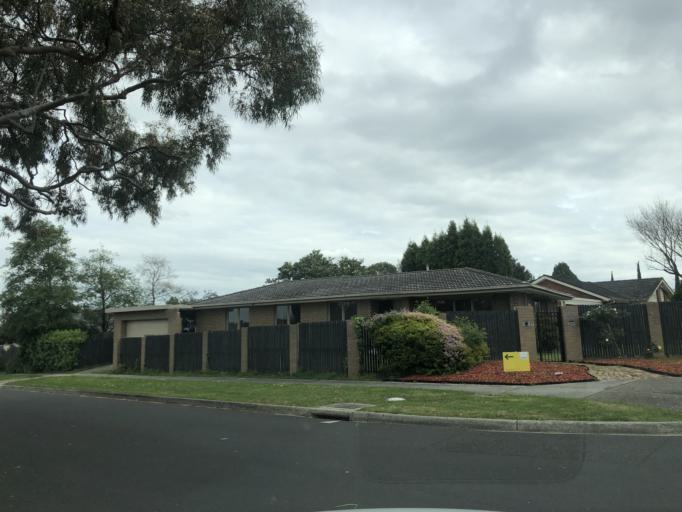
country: AU
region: Victoria
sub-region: Greater Dandenong
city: Noble Park North
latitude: -37.9347
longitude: 145.2001
